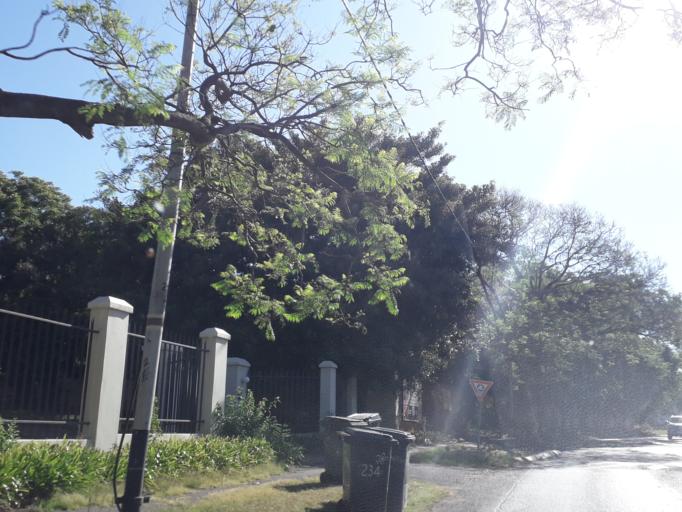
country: ZA
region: Gauteng
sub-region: City of Johannesburg Metropolitan Municipality
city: Roodepoort
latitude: -26.1359
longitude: 27.9666
